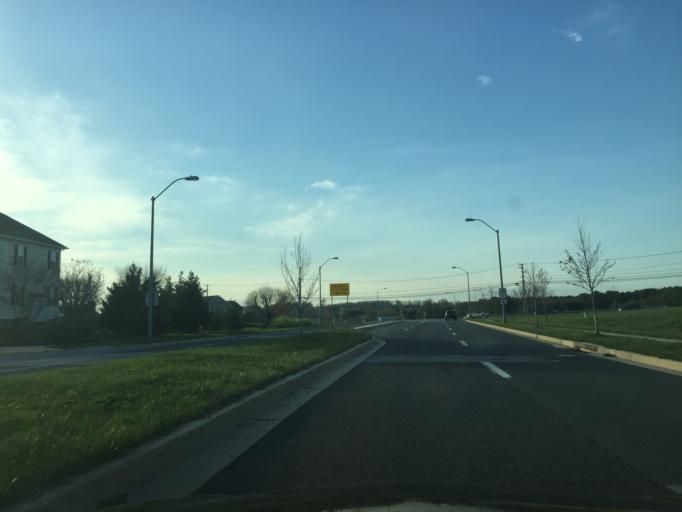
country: US
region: Maryland
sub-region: Baltimore County
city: Perry Hall
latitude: 39.4154
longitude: -76.4528
